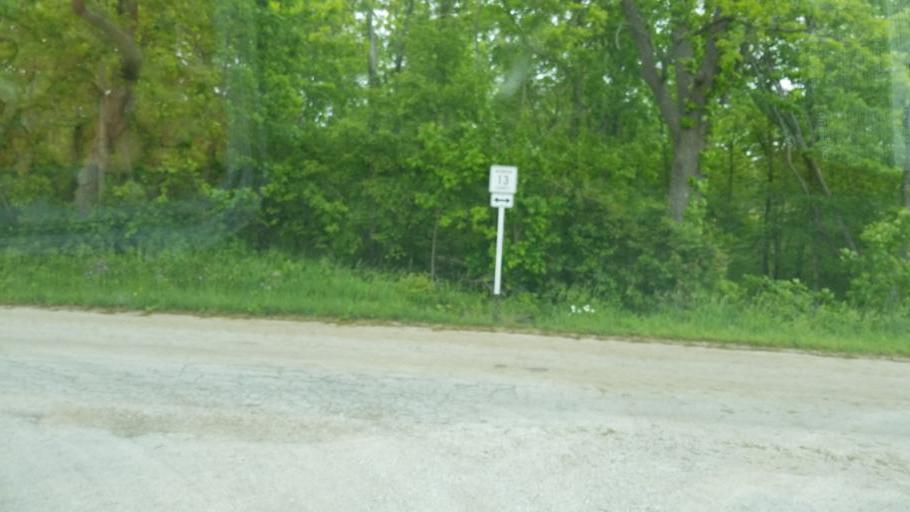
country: US
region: Ohio
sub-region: Knox County
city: Centerburg
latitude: 40.3501
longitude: -82.7568
